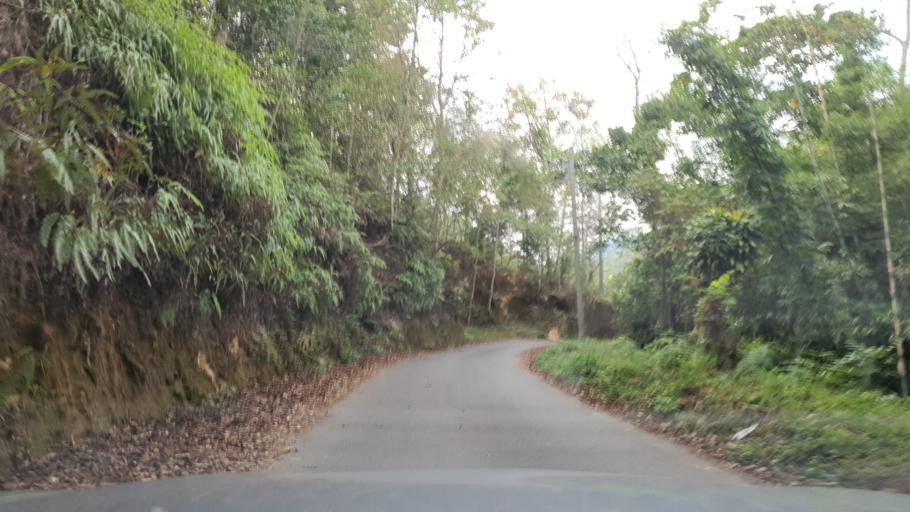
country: TH
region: Chiang Mai
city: Mae On
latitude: 18.9444
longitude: 99.3593
